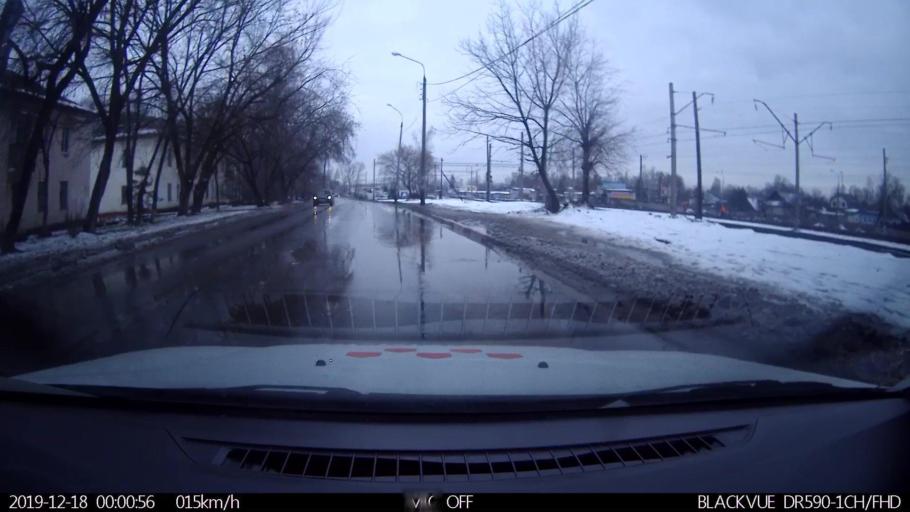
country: RU
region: Nizjnij Novgorod
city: Gorbatovka
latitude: 56.3678
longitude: 43.8271
